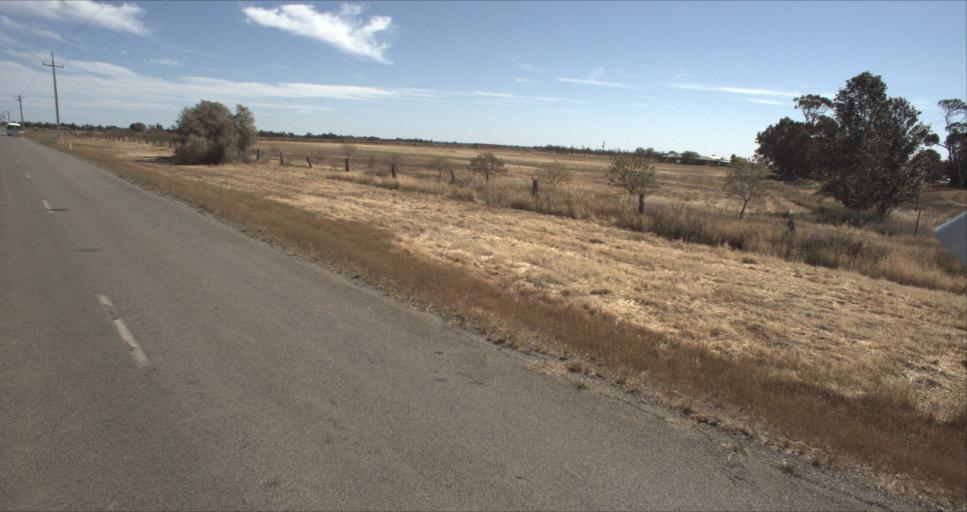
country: AU
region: New South Wales
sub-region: Leeton
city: Leeton
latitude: -34.5699
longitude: 146.3819
